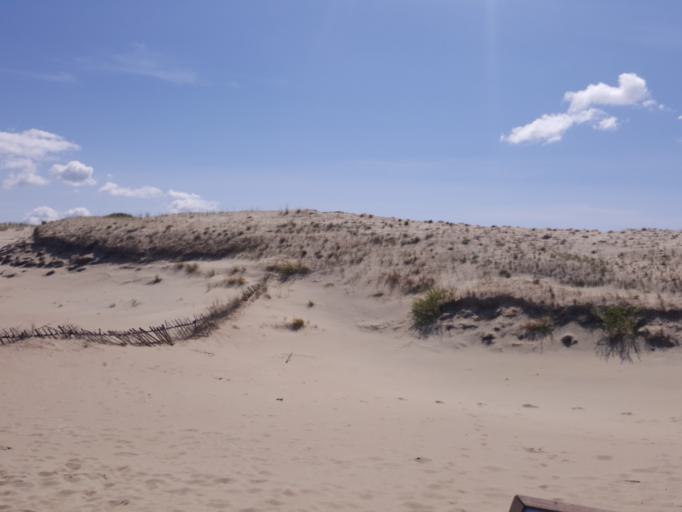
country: LT
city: Neringa
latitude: 55.4398
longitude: 21.0803
